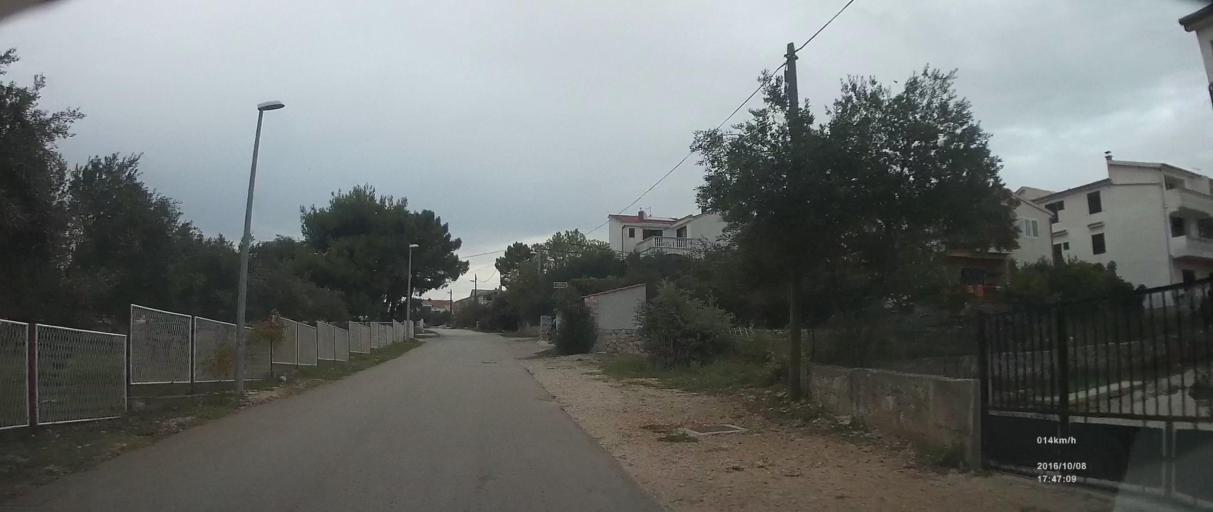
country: HR
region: Zadarska
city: Pakostane
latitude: 43.9135
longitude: 15.5033
